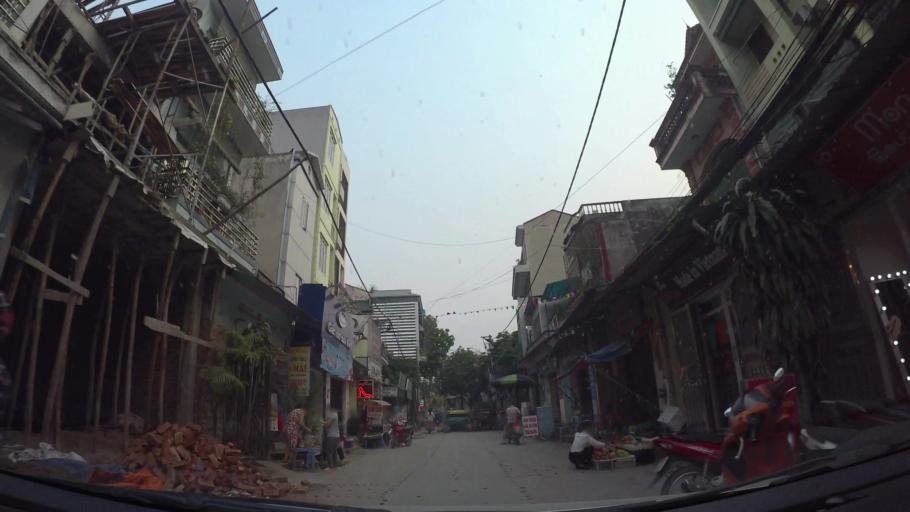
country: VN
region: Ha Noi
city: Ha Dong
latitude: 20.9924
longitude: 105.7298
